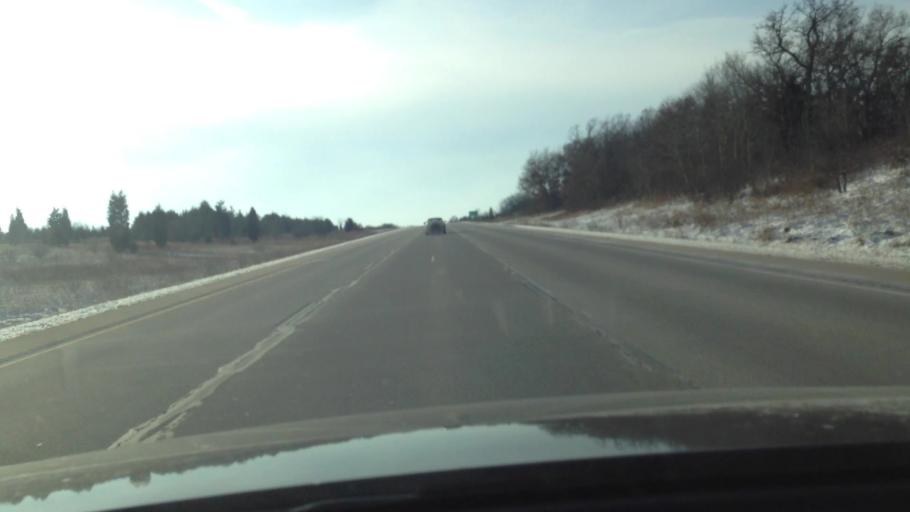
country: US
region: Wisconsin
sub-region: Walworth County
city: East Troy
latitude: 42.7704
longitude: -88.4183
